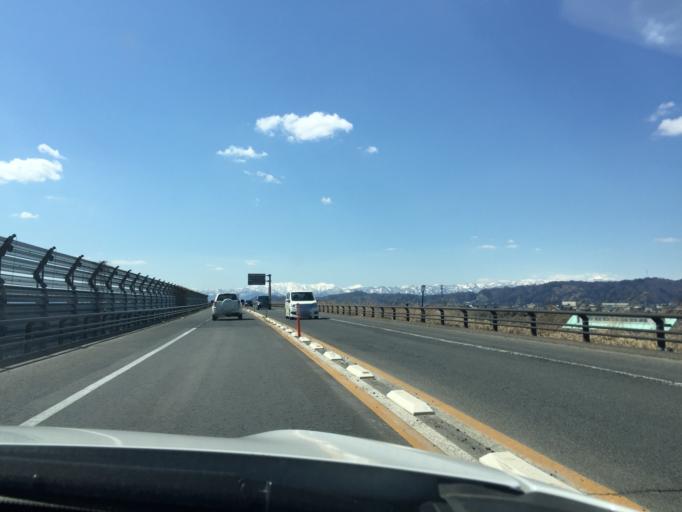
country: JP
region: Yamagata
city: Takahata
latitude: 38.0352
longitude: 140.1514
